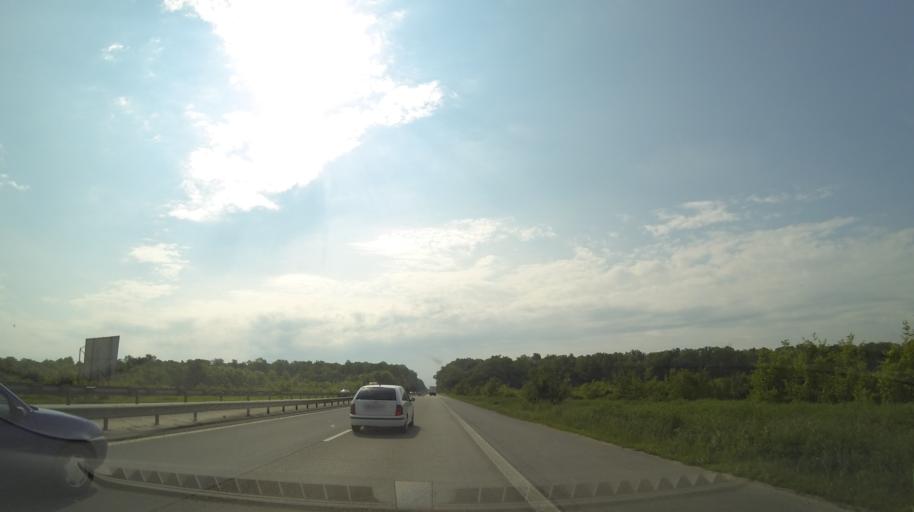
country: RO
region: Giurgiu
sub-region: Comuna Vanatorii Mici
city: Vanatorii Mici
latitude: 44.5139
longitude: 25.5622
